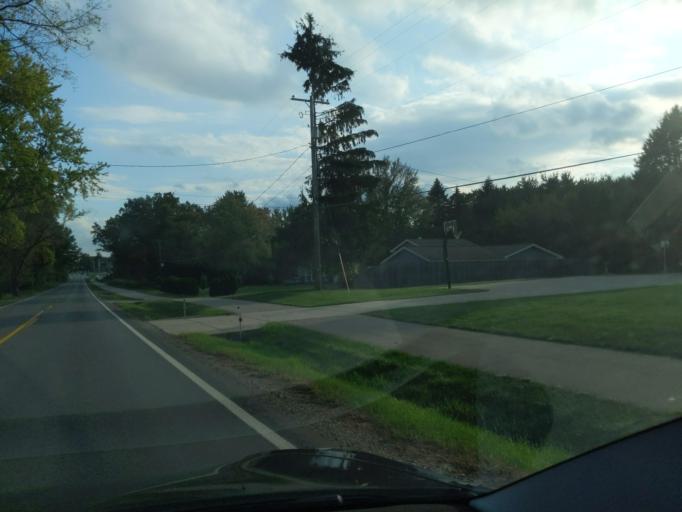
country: US
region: Michigan
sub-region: Jackson County
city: Jackson
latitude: 42.3269
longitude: -84.4629
